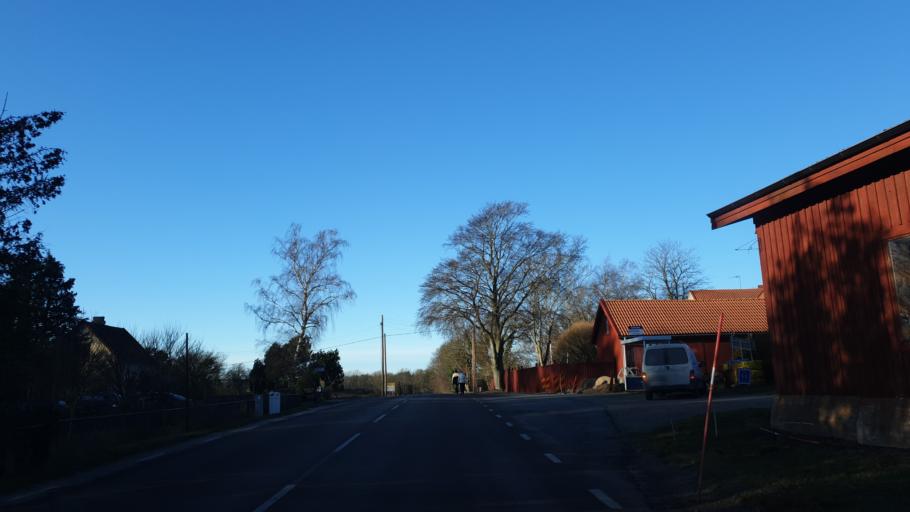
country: SE
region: Blekinge
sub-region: Ronneby Kommun
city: Ronneby
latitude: 56.1970
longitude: 15.3320
